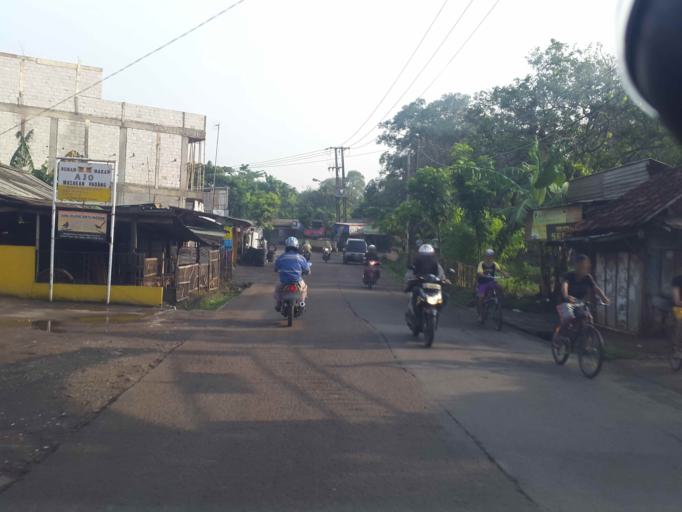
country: ID
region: West Java
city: Bekasi
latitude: -6.3075
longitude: 107.0289
